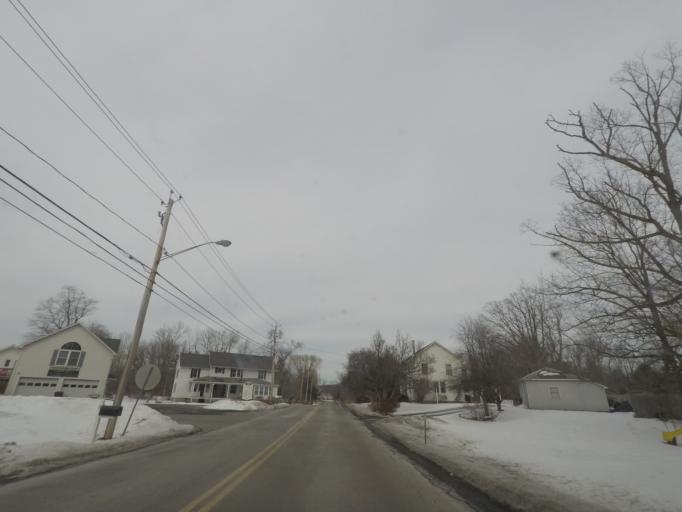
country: US
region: New York
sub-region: Albany County
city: Voorheesville
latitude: 42.6563
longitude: -73.9287
